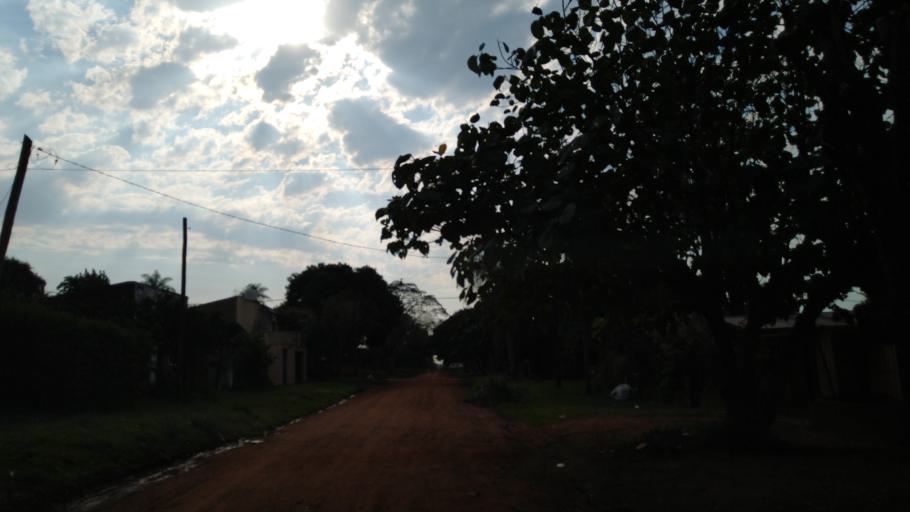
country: AR
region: Misiones
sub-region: Departamento de Capital
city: Posadas
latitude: -27.4294
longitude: -55.8760
